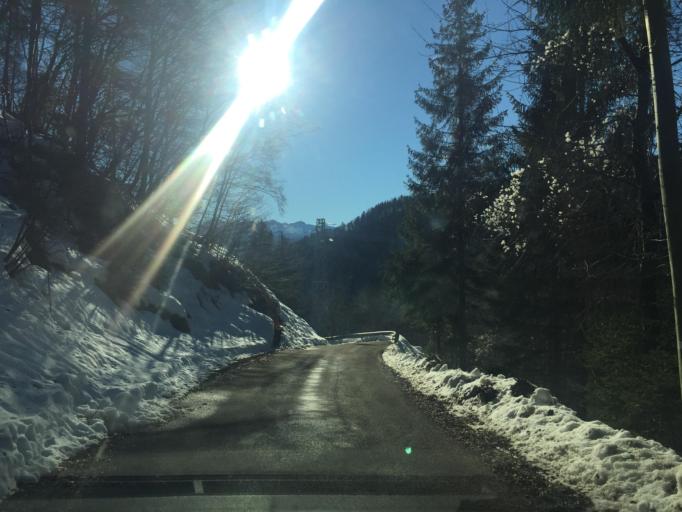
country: IT
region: Friuli Venezia Giulia
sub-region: Provincia di Udine
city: Lauco
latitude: 46.4455
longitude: 12.9345
